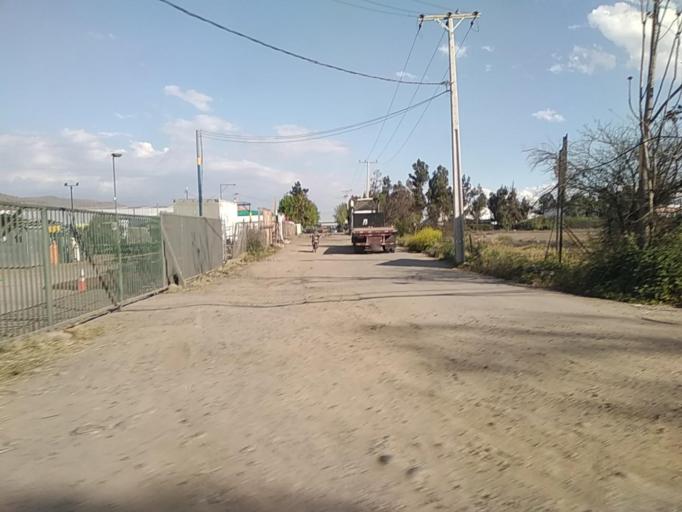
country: CL
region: Santiago Metropolitan
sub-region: Provincia de Chacabuco
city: Chicureo Abajo
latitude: -33.3126
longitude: -70.7219
